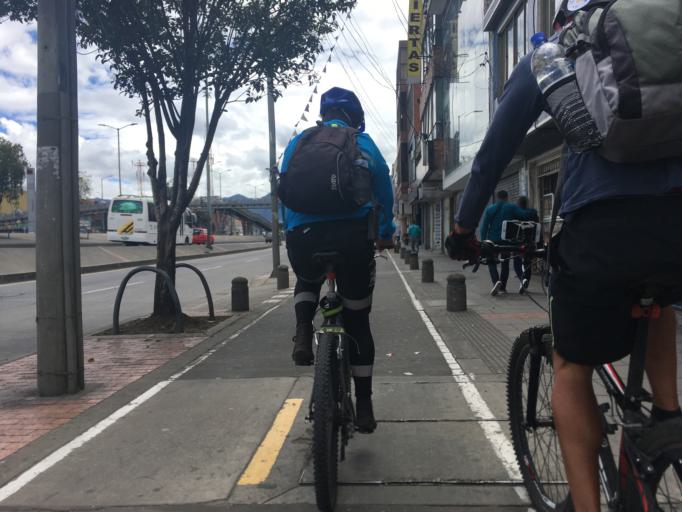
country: CO
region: Bogota D.C.
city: Bogota
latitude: 4.5944
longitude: -74.1363
